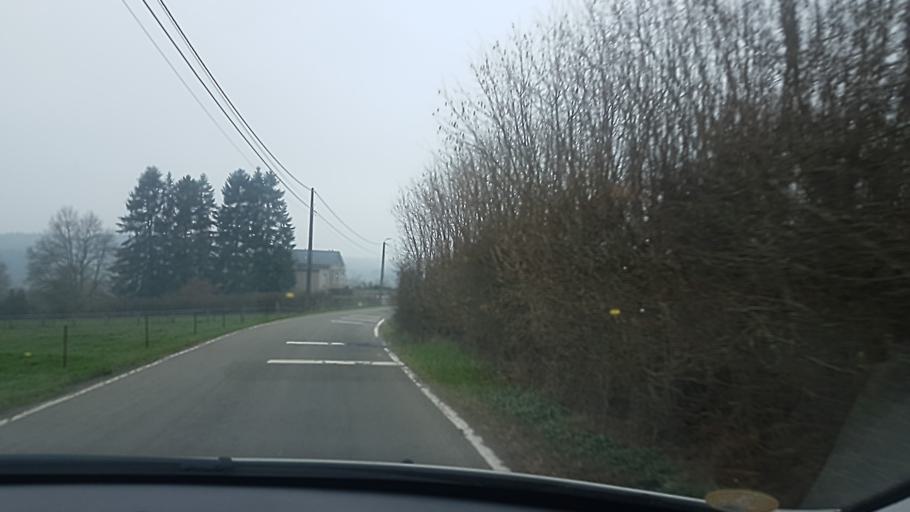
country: FR
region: Champagne-Ardenne
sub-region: Departement des Ardennes
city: Haybes
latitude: 50.0249
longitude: 4.6461
